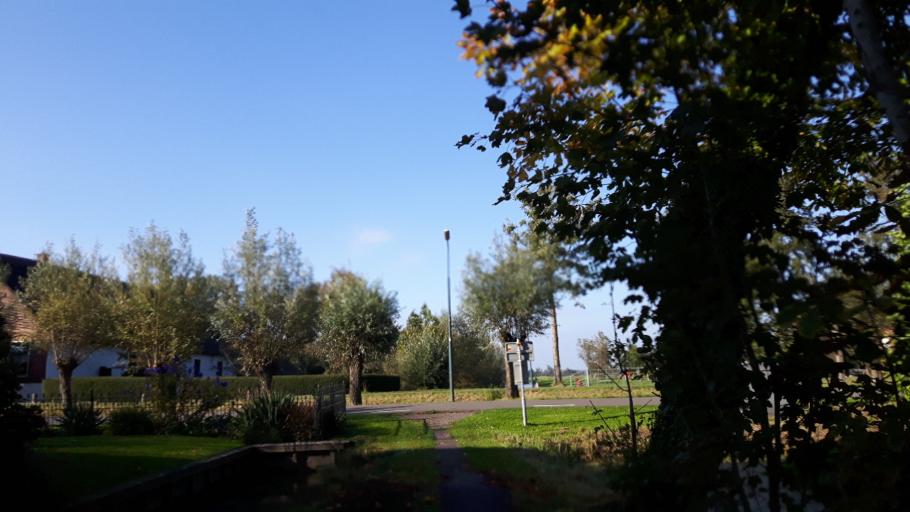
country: NL
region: Utrecht
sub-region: Gemeente Oudewater
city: Oudewater
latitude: 51.9874
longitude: 4.8815
